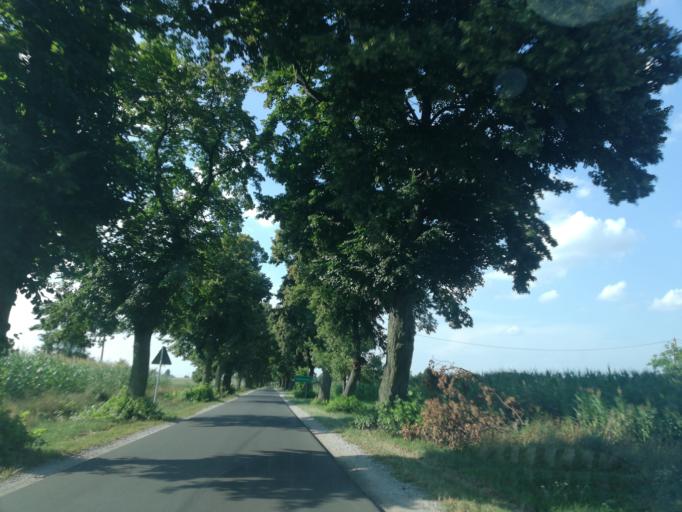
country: PL
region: Kujawsko-Pomorskie
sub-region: Powiat golubsko-dobrzynski
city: Ciechocin
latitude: 53.1048
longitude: 18.9123
